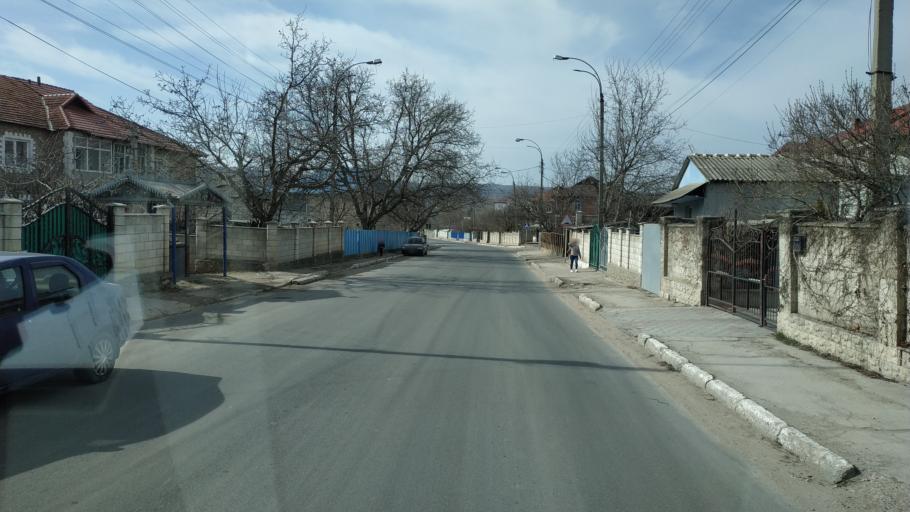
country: MD
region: Chisinau
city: Vatra
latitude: 47.0940
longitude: 28.6704
